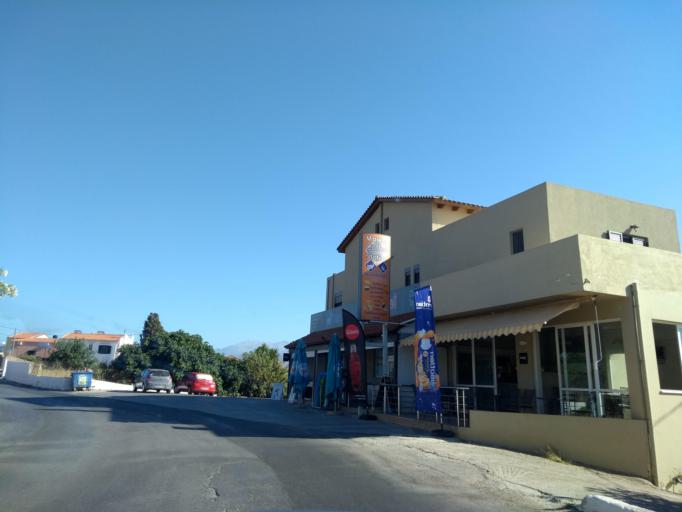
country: GR
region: Crete
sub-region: Nomos Chanias
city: Pithari
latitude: 35.5633
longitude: 24.0919
